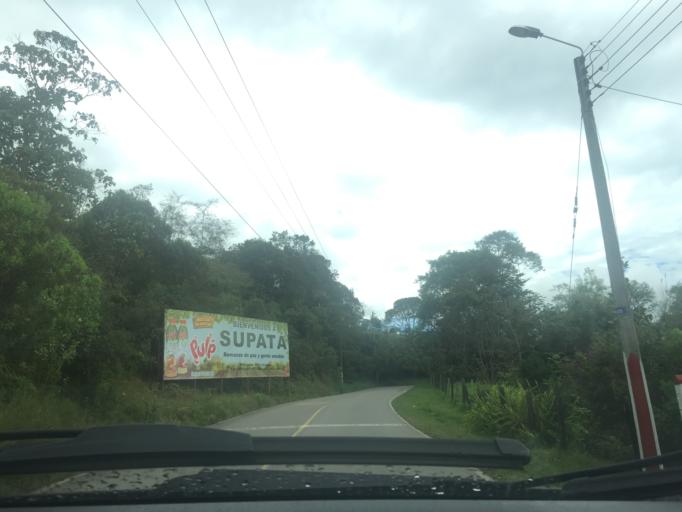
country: CO
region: Cundinamarca
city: Supata
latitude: 5.0353
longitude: -74.2691
